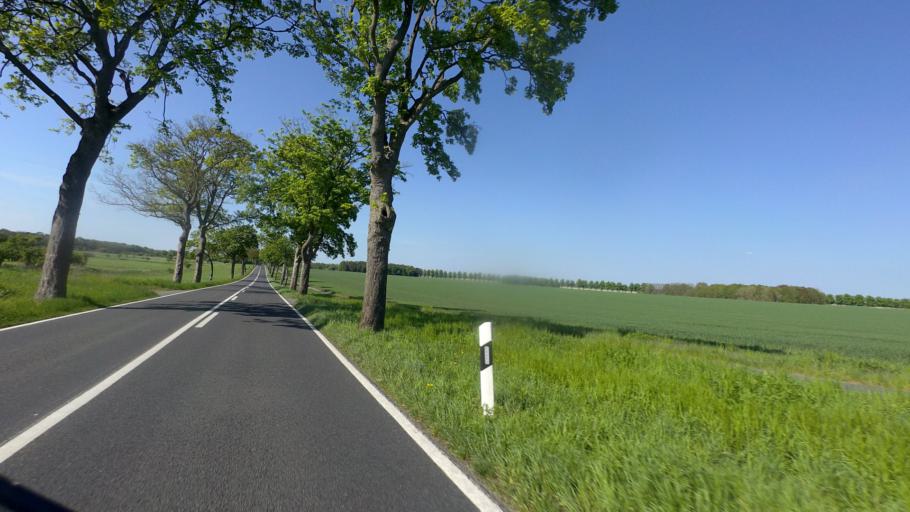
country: DE
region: Brandenburg
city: Mittenwalde
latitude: 52.2945
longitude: 13.5203
